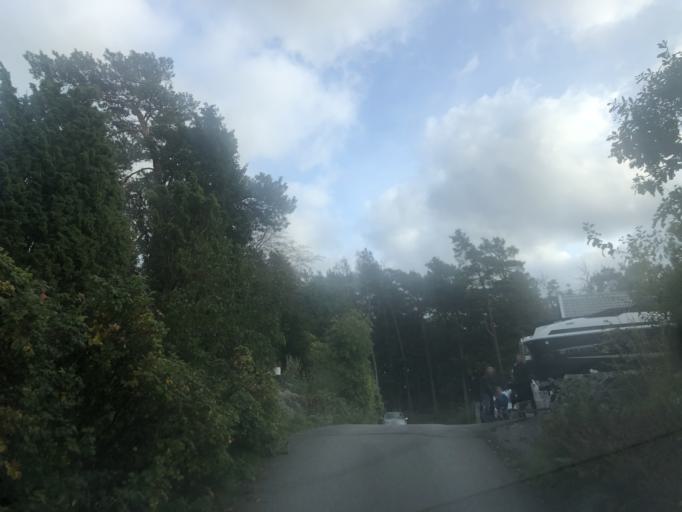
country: SE
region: Vaestra Goetaland
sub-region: Goteborg
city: Billdal
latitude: 57.6281
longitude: 11.9472
